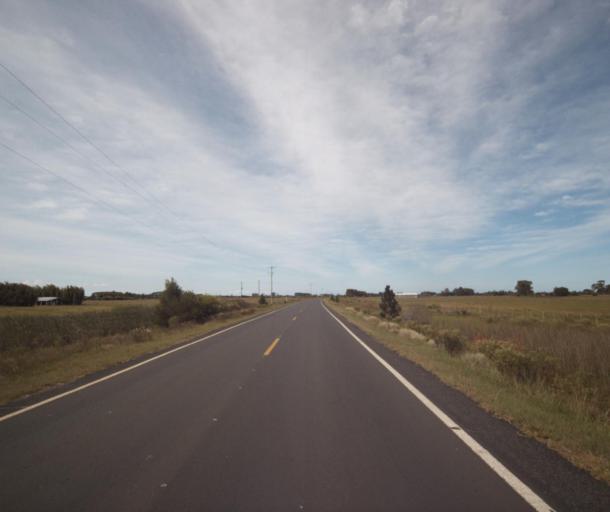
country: BR
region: Rio Grande do Sul
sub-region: Rio Grande
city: Rio Grande
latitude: -31.9285
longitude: -51.9588
